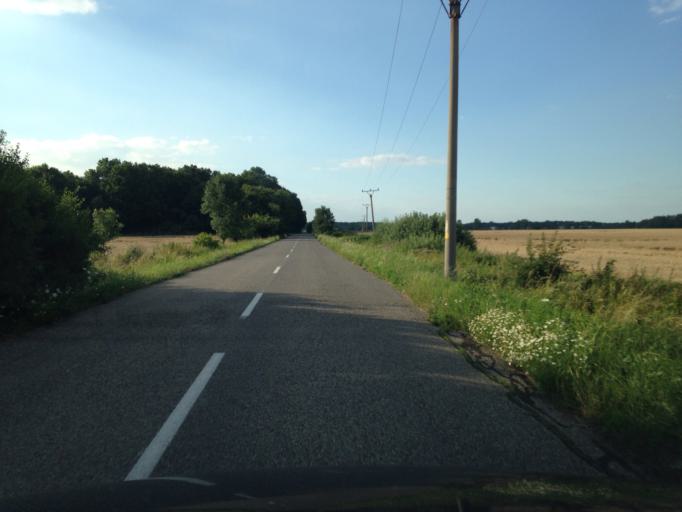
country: AT
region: Lower Austria
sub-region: Politischer Bezirk Ganserndorf
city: Angern an der March
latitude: 48.3932
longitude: 16.8638
